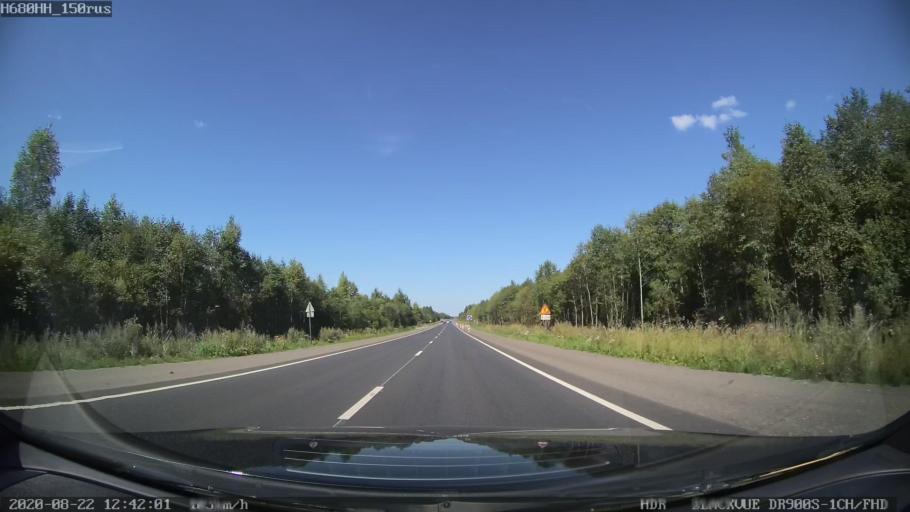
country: RU
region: Tverskaya
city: Rameshki
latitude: 57.3555
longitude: 36.0972
